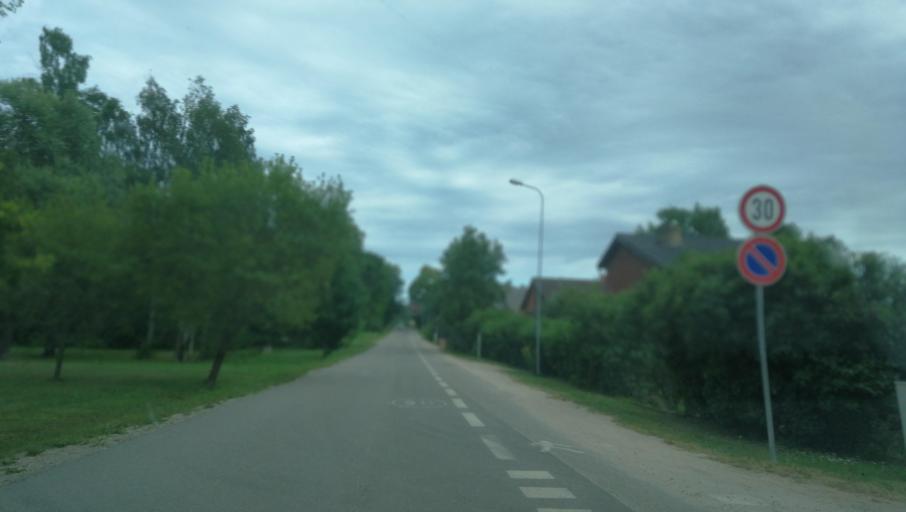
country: LV
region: Cesu Rajons
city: Cesis
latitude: 57.3020
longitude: 25.2830
